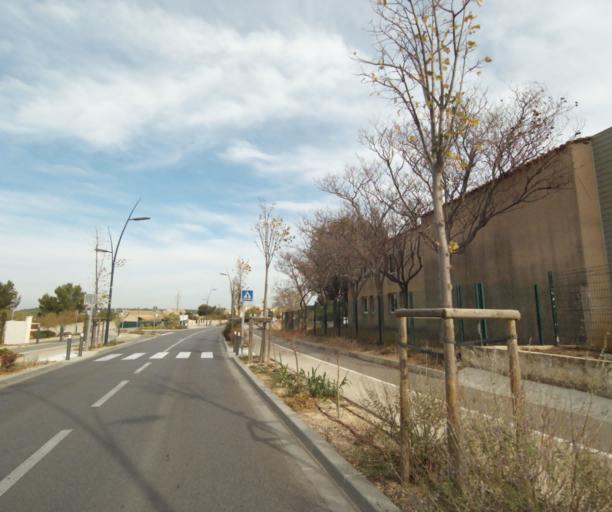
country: FR
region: Provence-Alpes-Cote d'Azur
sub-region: Departement des Bouches-du-Rhone
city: Gignac-la-Nerthe
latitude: 43.3898
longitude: 5.2315
